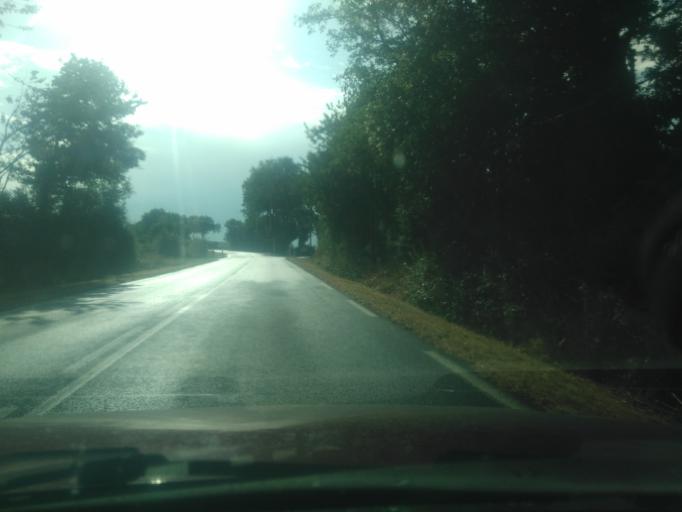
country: FR
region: Pays de la Loire
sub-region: Departement de la Vendee
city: Saint-Pierre-du-Chemin
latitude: 46.6436
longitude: -0.6276
